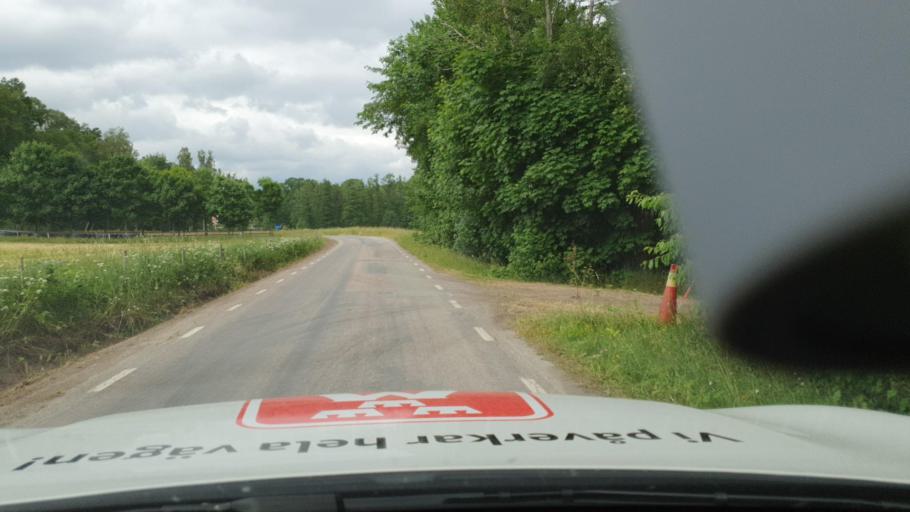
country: SE
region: Vaestra Goetaland
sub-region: Hjo Kommun
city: Hjo
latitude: 58.2236
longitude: 14.2054
